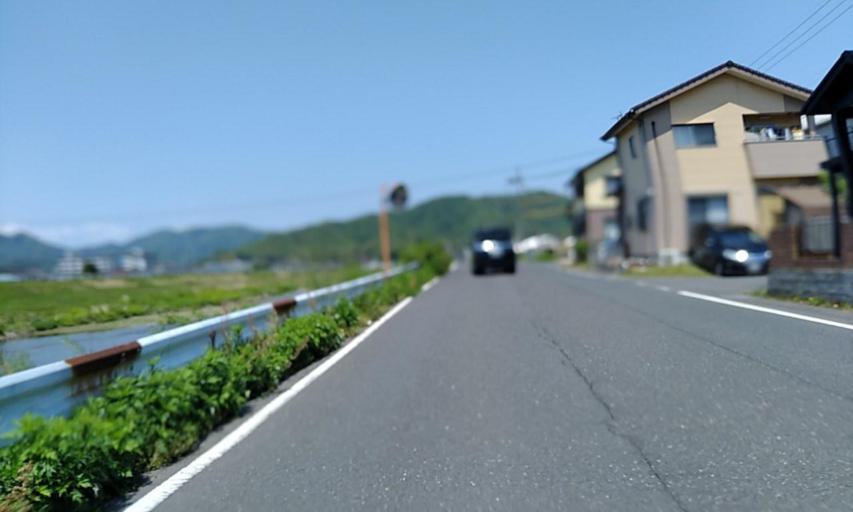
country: JP
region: Kyoto
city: Maizuru
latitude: 35.4378
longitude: 135.3360
